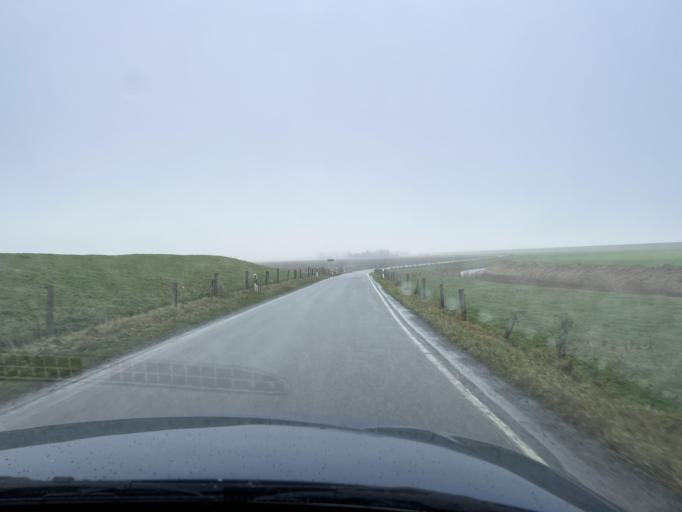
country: DE
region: Schleswig-Holstein
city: Schulp
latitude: 54.2639
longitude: 8.9290
